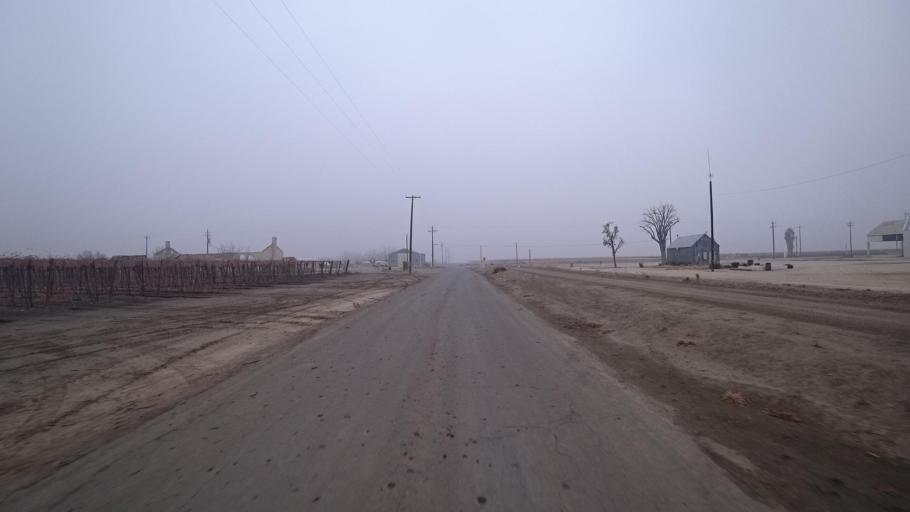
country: US
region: California
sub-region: Kern County
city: Buttonwillow
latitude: 35.4270
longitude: -119.5173
